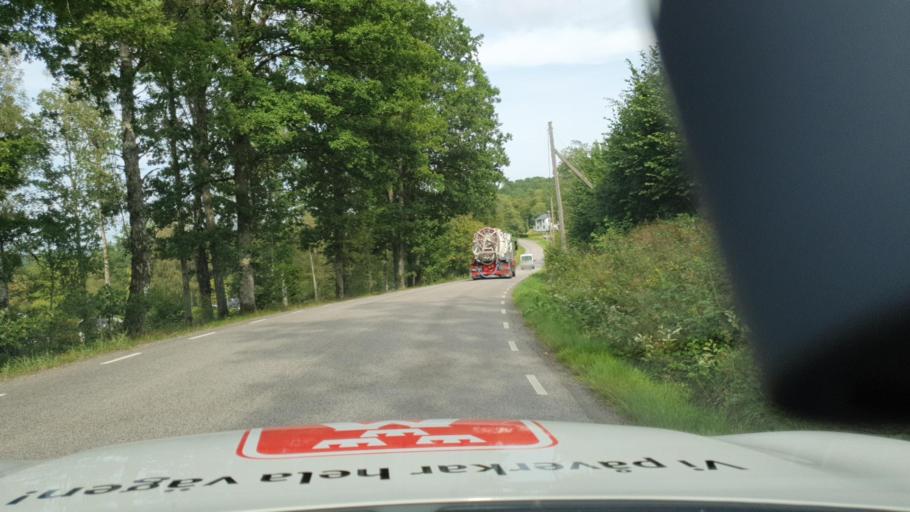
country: SE
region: Vaestra Goetaland
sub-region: Marks Kommun
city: Kinna
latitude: 57.4561
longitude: 12.7020
